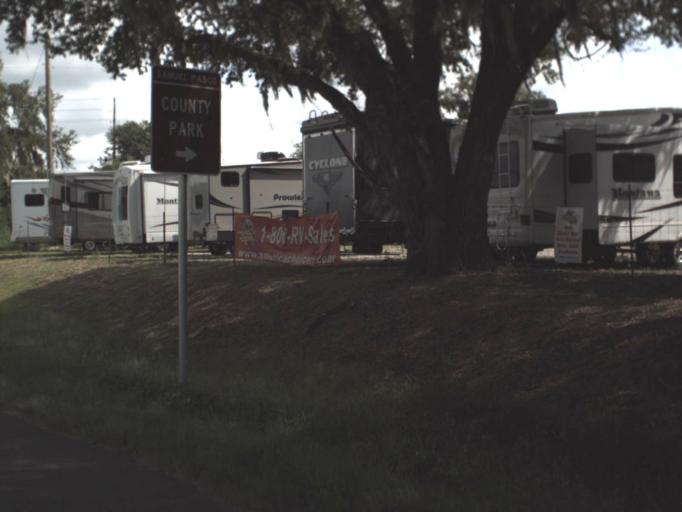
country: US
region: Florida
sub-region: Pasco County
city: Zephyrhills South
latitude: 28.2059
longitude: -82.1740
